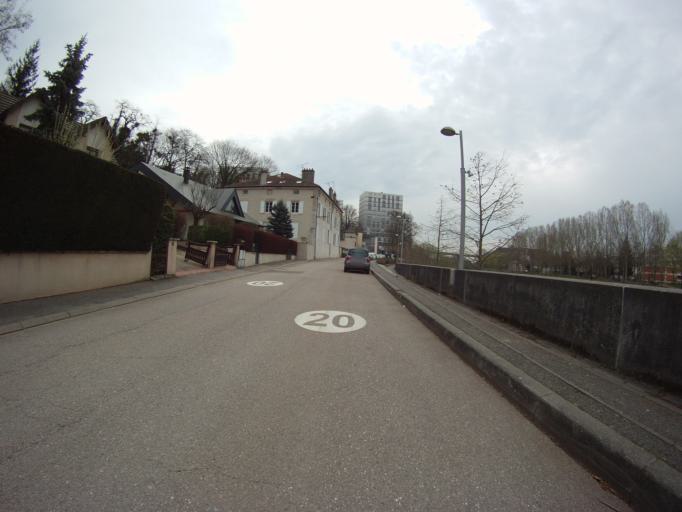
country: FR
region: Lorraine
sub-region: Departement de Meurthe-et-Moselle
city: Malzeville
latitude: 48.7053
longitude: 6.1886
